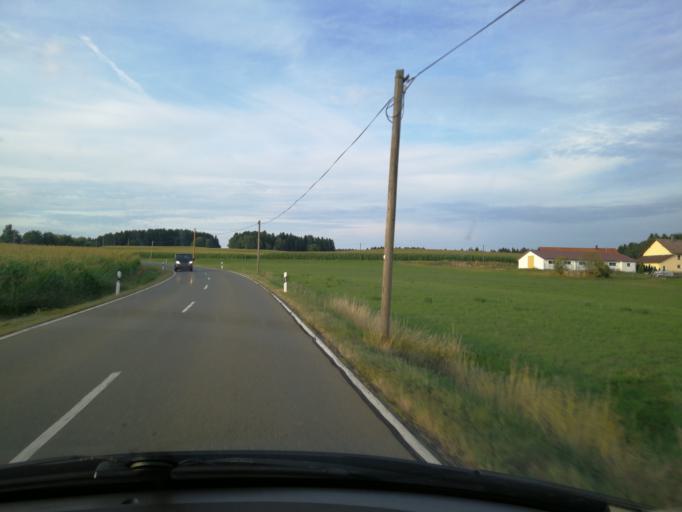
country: DE
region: Bavaria
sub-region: Lower Bavaria
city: Wiesenfelden
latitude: 49.0587
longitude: 12.5200
